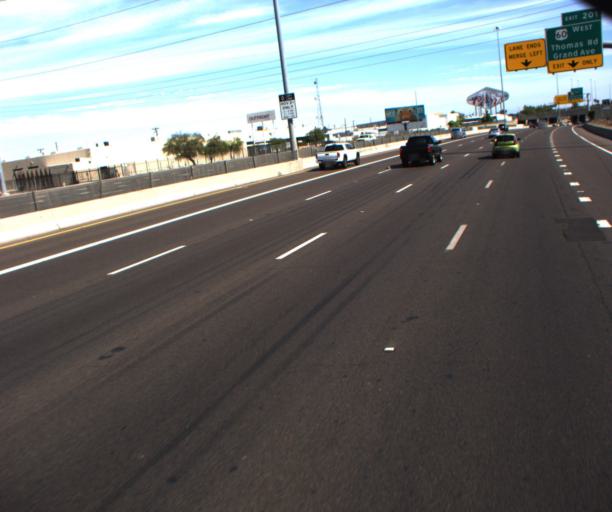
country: US
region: Arizona
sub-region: Maricopa County
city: Phoenix
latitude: 33.4729
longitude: -112.1126
